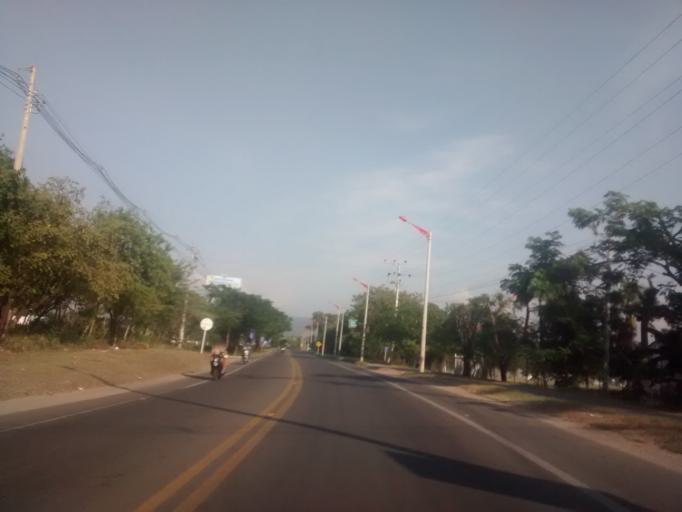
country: CO
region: Cundinamarca
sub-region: Girardot
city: Girardot City
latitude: 4.2957
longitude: -74.7888
